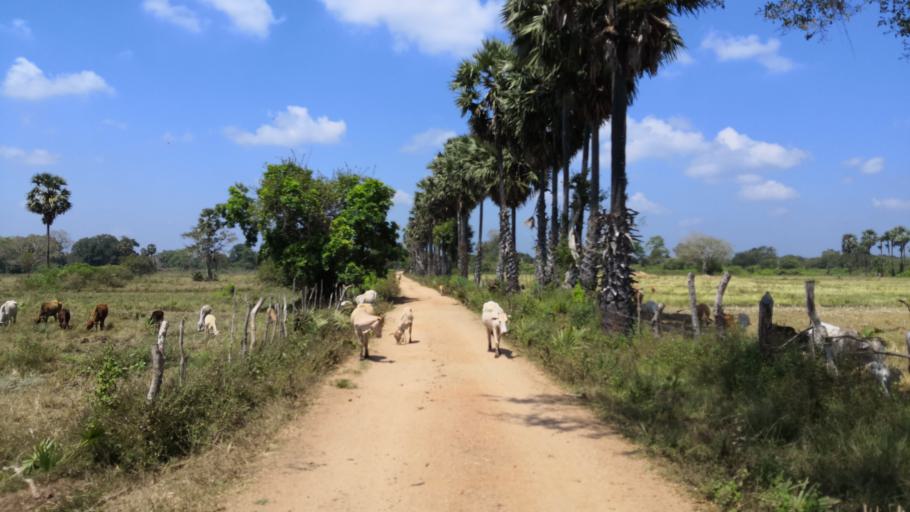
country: LK
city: Padaviya Divisional Secretariat
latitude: 8.9716
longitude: 80.6803
